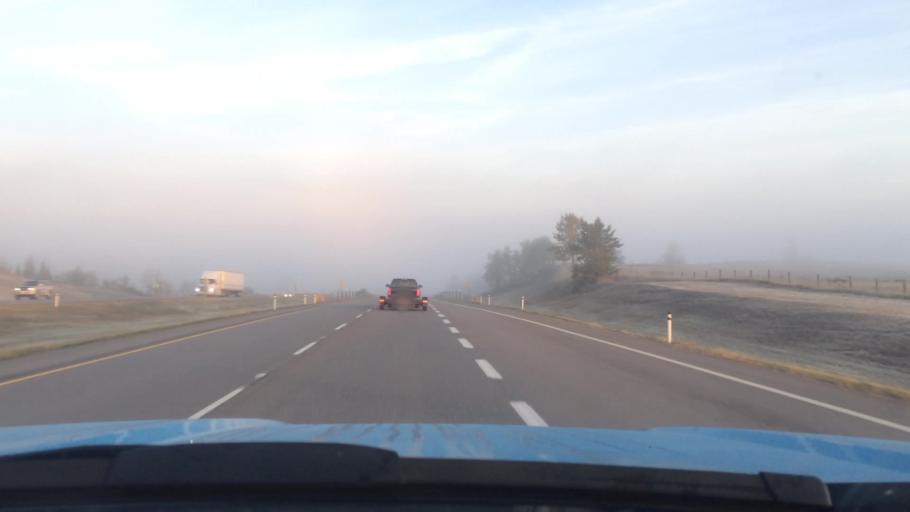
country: CA
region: Alberta
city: Cochrane
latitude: 51.0903
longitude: -114.5403
